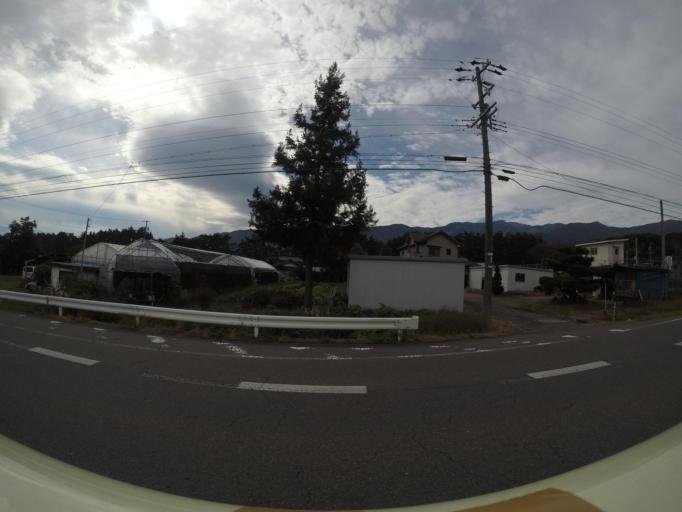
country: JP
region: Nagano
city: Ina
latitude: 35.8596
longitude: 137.9052
